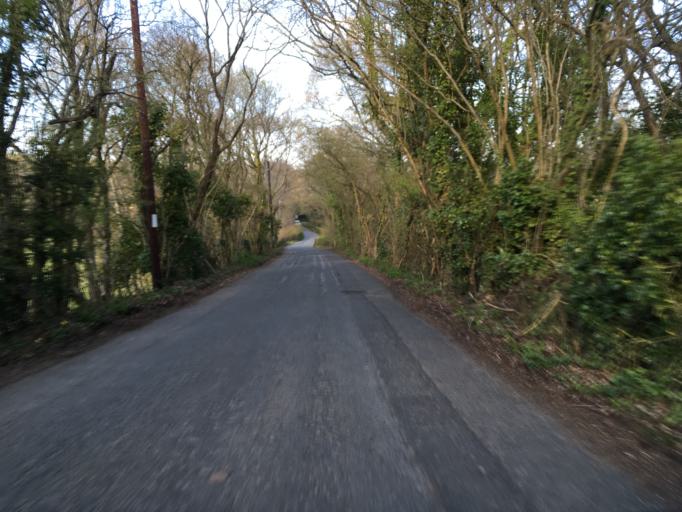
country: GB
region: Wales
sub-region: Torfaen County Borough
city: New Inn
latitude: 51.7145
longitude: -2.9613
